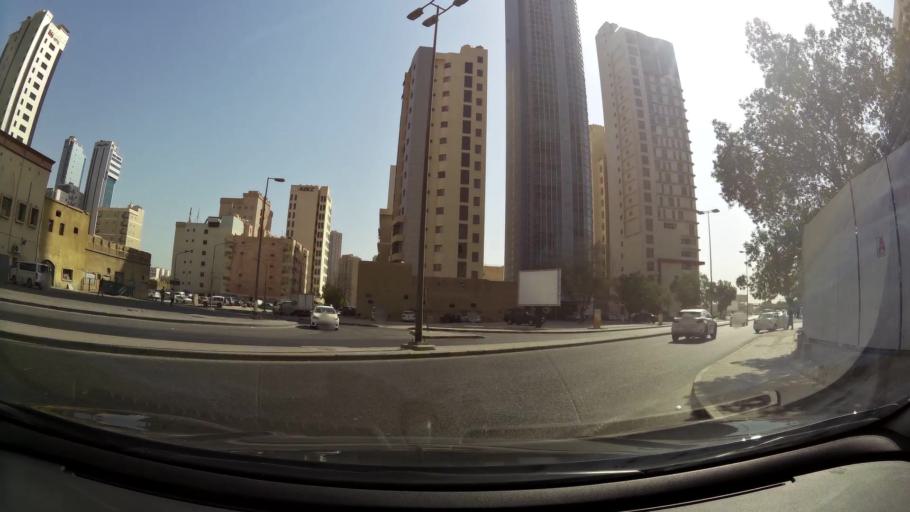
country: KW
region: Al Asimah
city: Ad Dasmah
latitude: 29.3773
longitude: 47.9928
